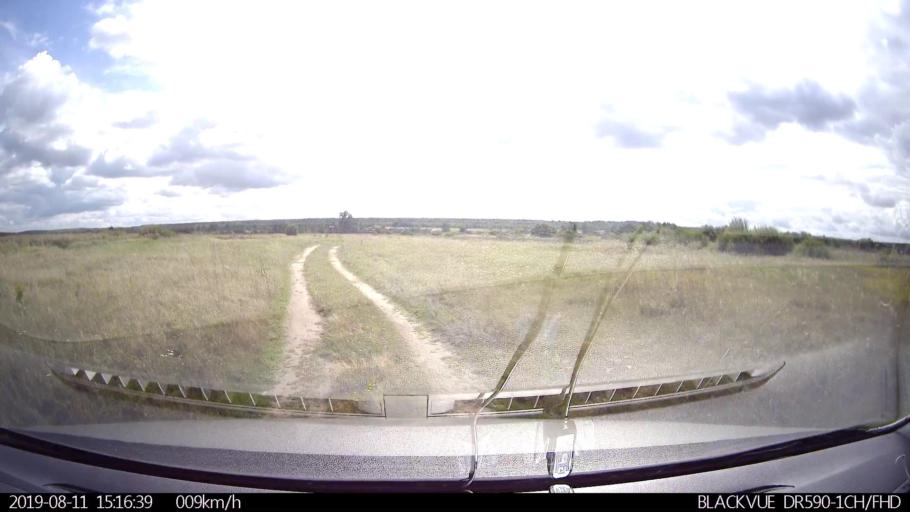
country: RU
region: Ulyanovsk
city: Ignatovka
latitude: 53.8475
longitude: 47.5883
